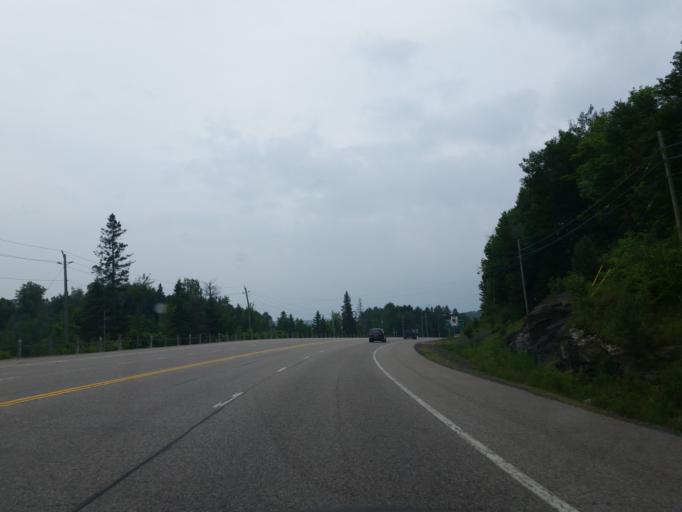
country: CA
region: Ontario
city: Huntsville
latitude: 45.3495
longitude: -79.1498
